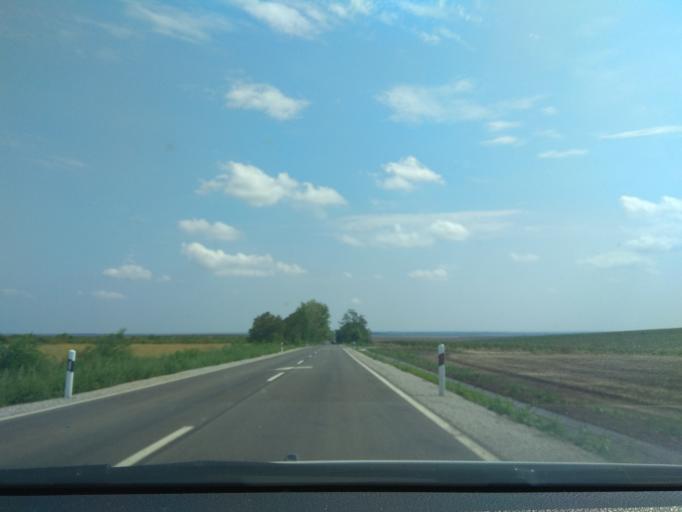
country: HU
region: Heves
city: Andornaktalya
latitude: 47.8340
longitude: 20.4348
